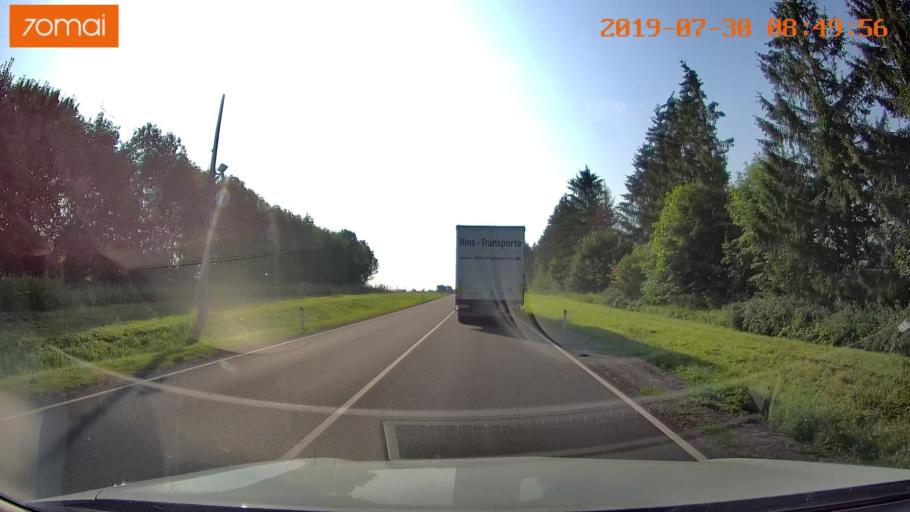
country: RU
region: Kaliningrad
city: Chernyakhovsk
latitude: 54.6102
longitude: 21.9308
